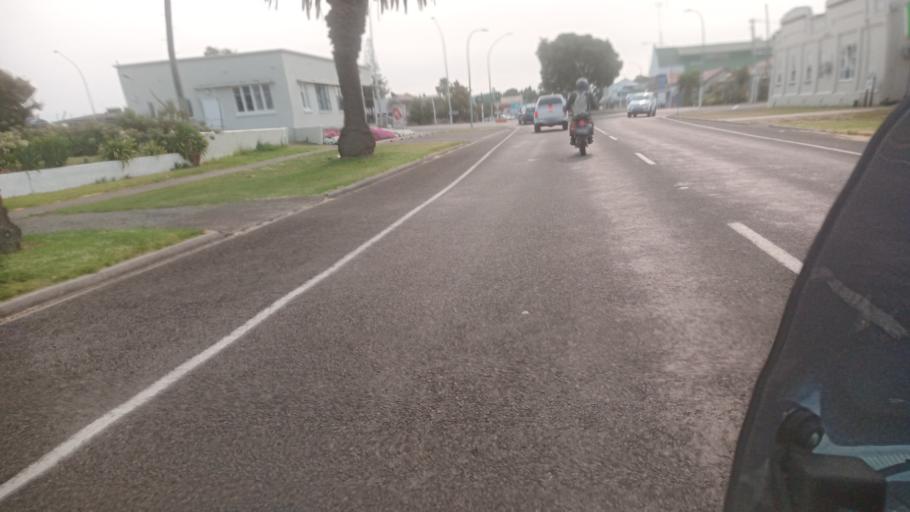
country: NZ
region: Bay of Plenty
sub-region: Opotiki District
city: Opotiki
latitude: -38.0043
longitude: 177.2880
